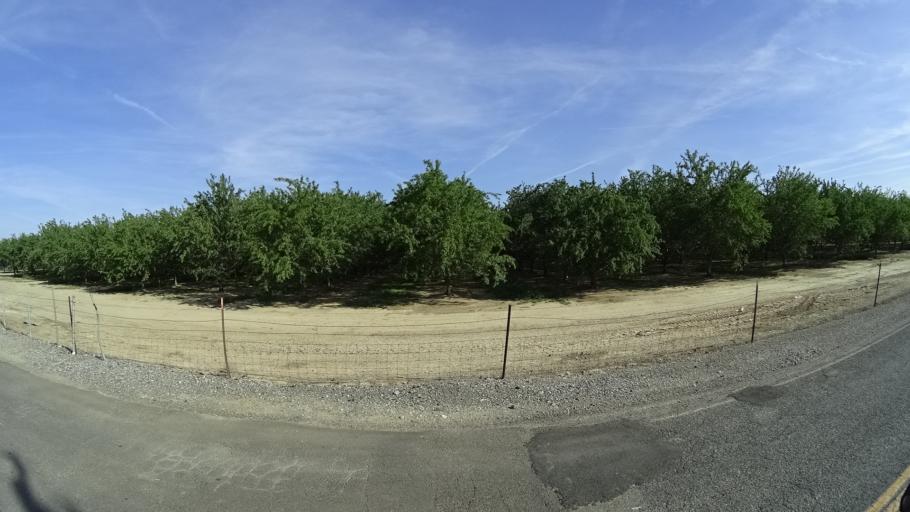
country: US
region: California
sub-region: Glenn County
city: Orland
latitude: 39.6678
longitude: -122.2015
